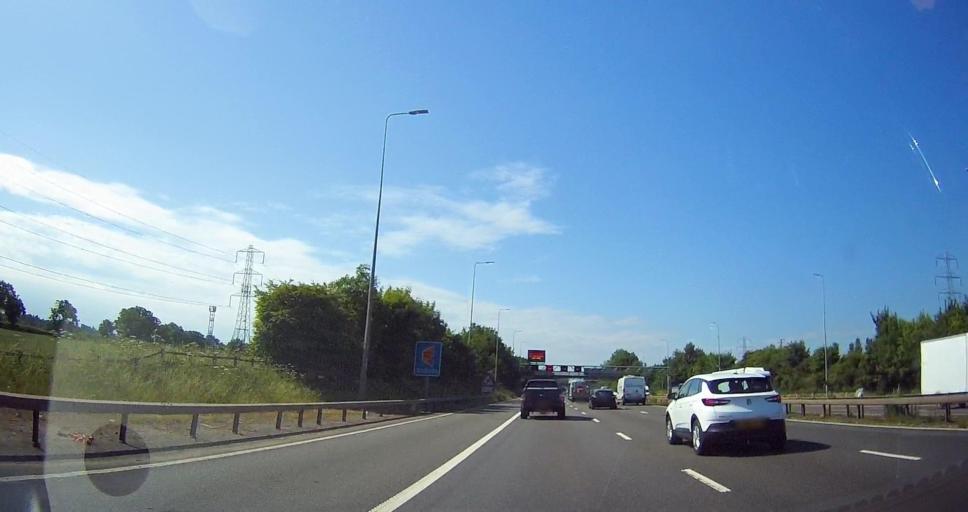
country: GB
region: England
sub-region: Solihull
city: Hampton in Arden
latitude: 52.4346
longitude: -1.7112
